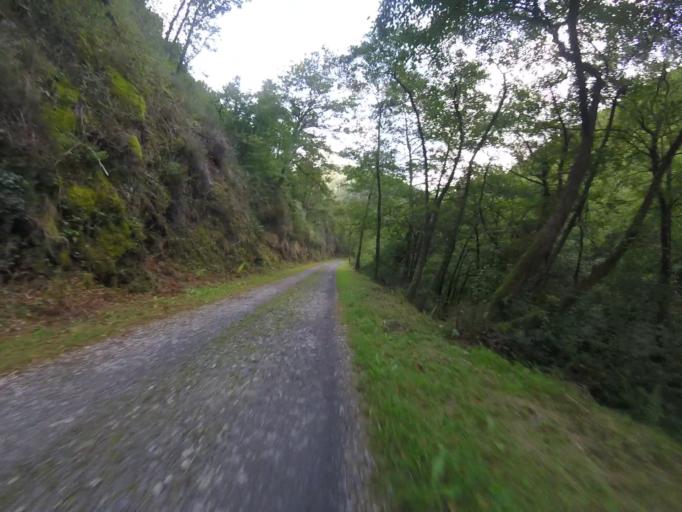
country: ES
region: Basque Country
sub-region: Provincia de Guipuzcoa
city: Berastegui
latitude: 43.1519
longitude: -1.9641
